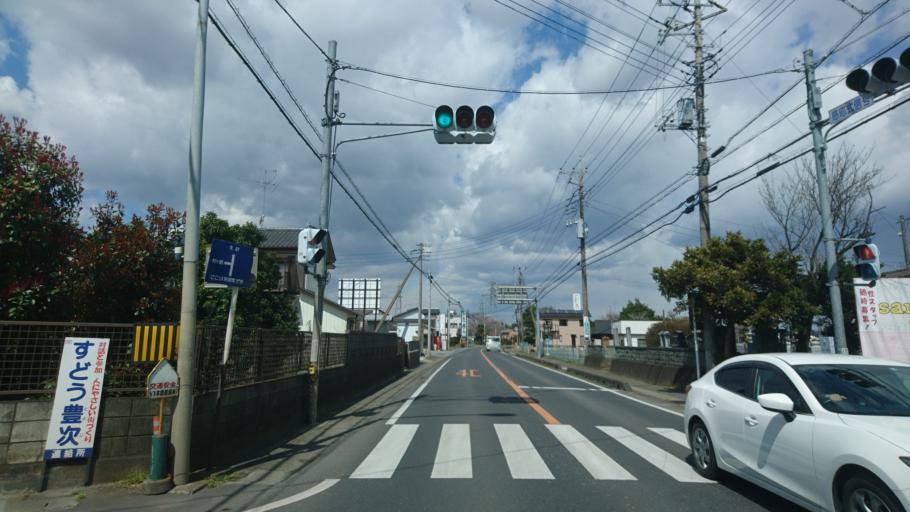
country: JP
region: Ibaraki
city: Ishige
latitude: 36.2067
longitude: 139.9409
